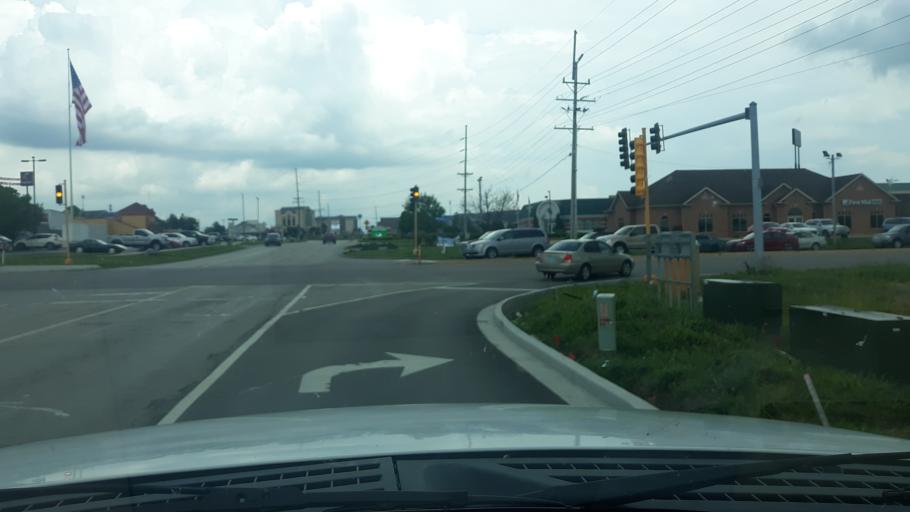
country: US
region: Illinois
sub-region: Williamson County
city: Marion
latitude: 37.7451
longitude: -88.9704
